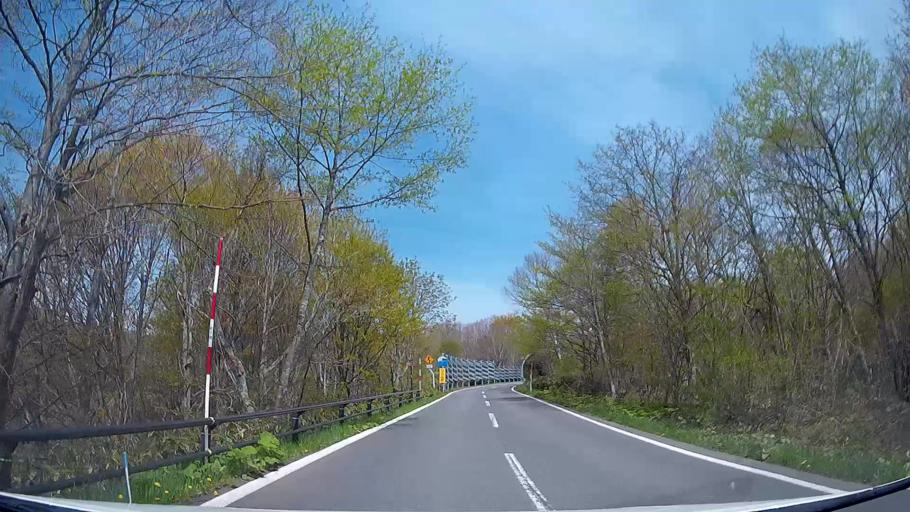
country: JP
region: Iwate
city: Shizukuishi
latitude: 39.9254
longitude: 140.9624
